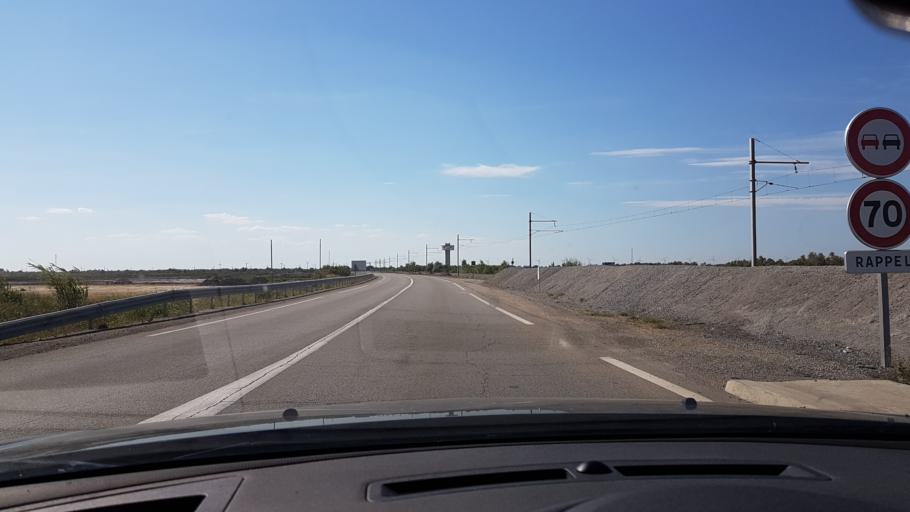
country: FR
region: Provence-Alpes-Cote d'Azur
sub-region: Departement des Bouches-du-Rhone
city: Port-Saint-Louis-du-Rhone
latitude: 43.4148
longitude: 4.8197
